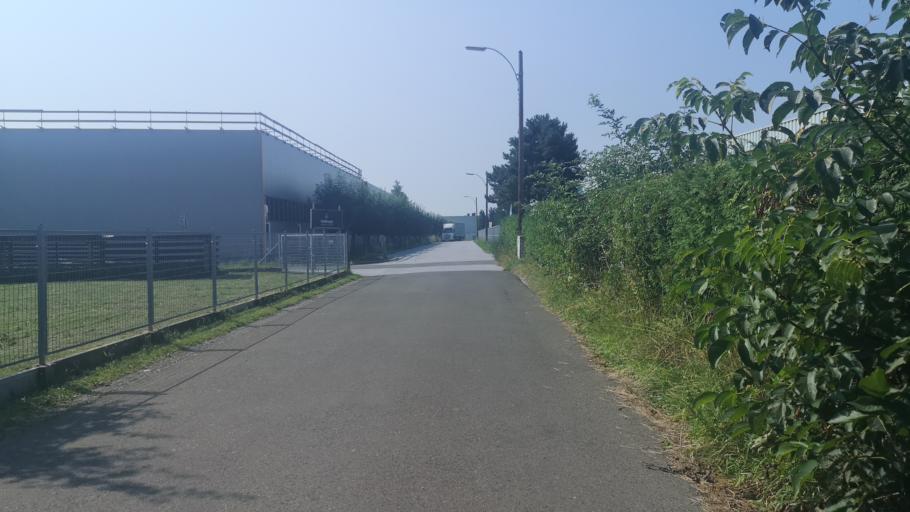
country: AT
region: Styria
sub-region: Politischer Bezirk Graz-Umgebung
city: Seiersberg
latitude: 47.0229
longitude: 15.4083
